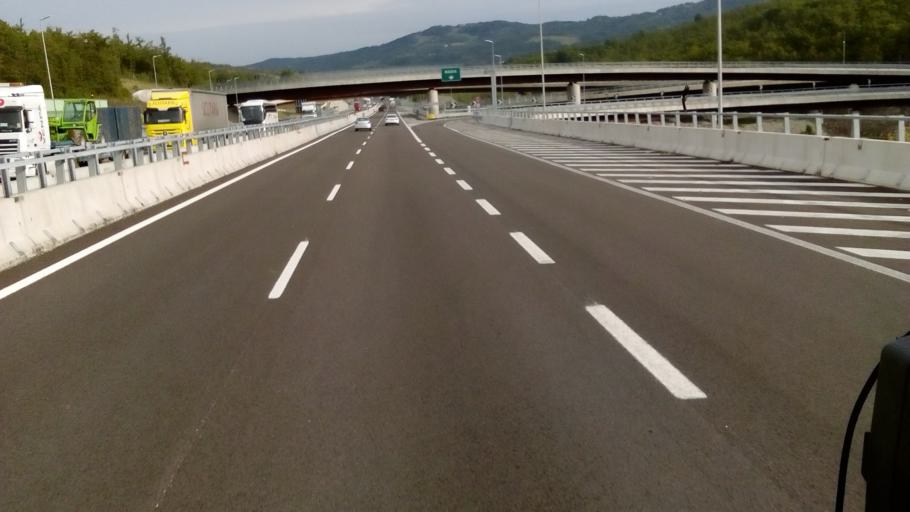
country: IT
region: Emilia-Romagna
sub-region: Provincia di Bologna
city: Castiglione dei Pepoli
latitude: 44.1540
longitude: 11.1951
